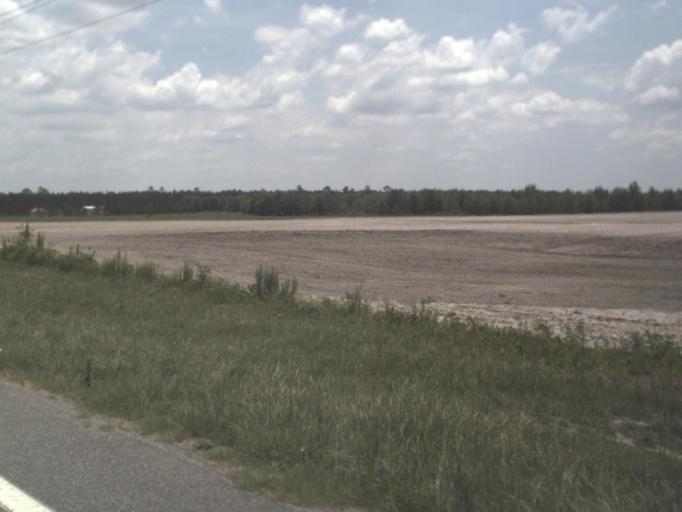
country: US
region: Florida
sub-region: Hamilton County
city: Jasper
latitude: 30.4898
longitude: -83.1610
